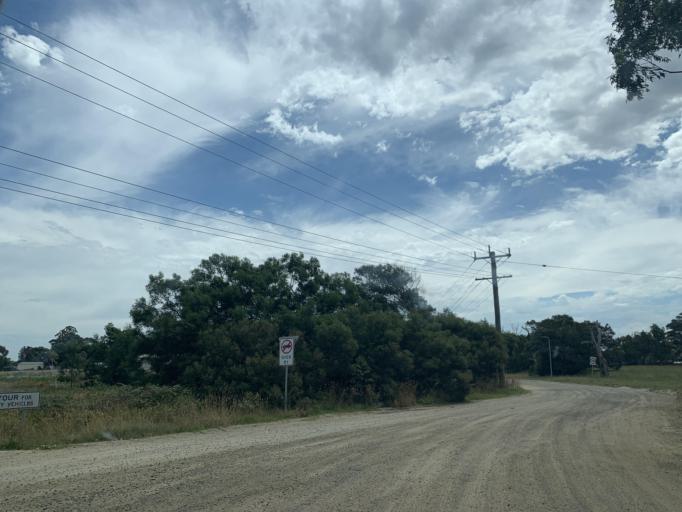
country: AU
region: Victoria
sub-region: Casey
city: Junction Village
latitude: -38.1348
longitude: 145.3337
